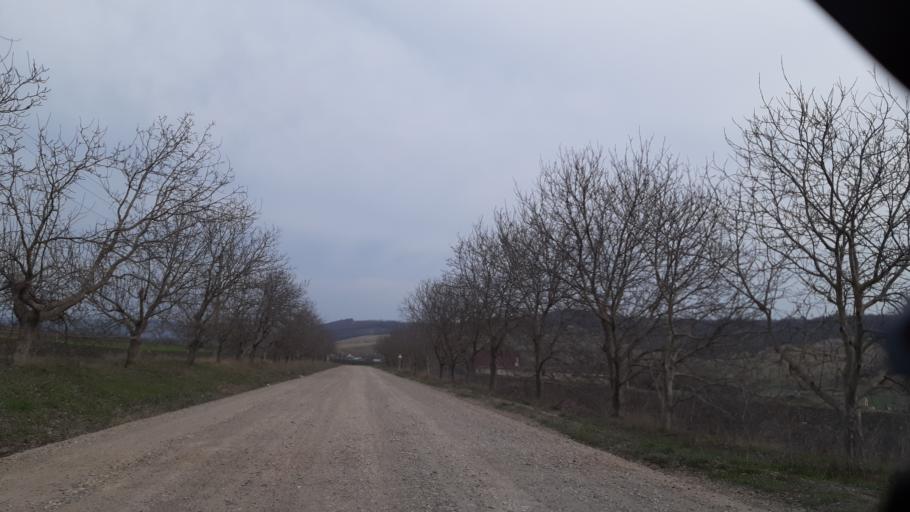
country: MD
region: Soldanesti
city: Soldanesti
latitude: 47.6900
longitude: 28.7418
